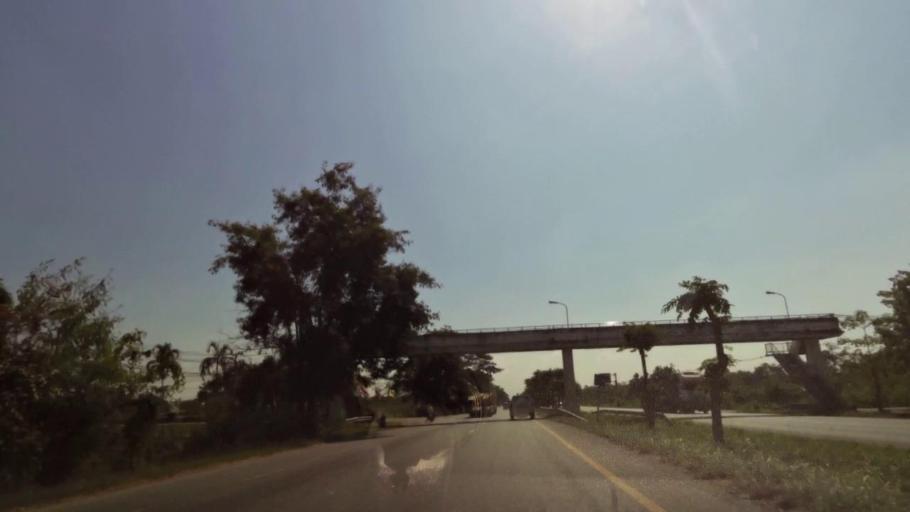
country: TH
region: Nakhon Sawan
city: Kao Liao
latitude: 15.7942
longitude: 100.1207
